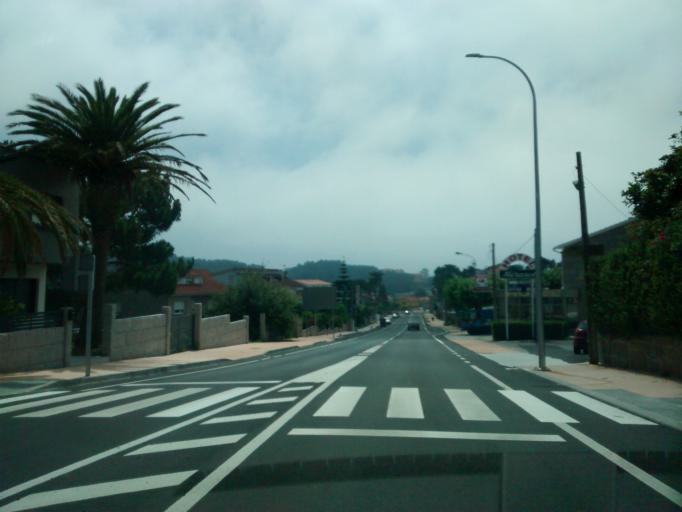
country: ES
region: Galicia
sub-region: Provincia de Pontevedra
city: Sanxenxo
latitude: 42.4217
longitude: -8.8737
